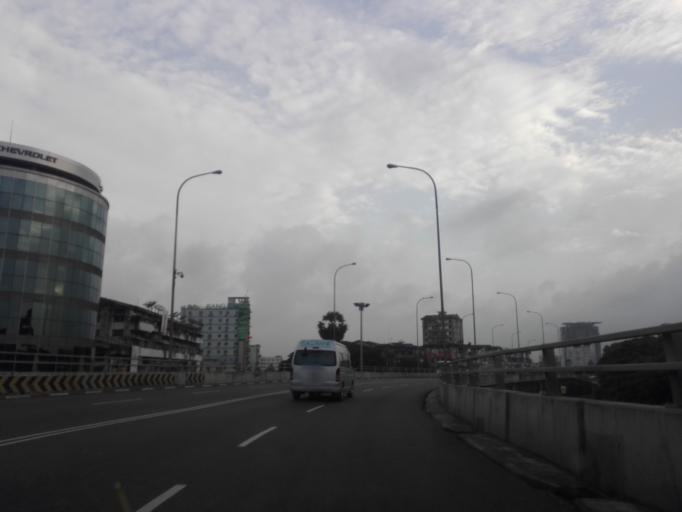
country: MM
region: Yangon
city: Yangon
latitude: 16.8262
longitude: 96.1309
